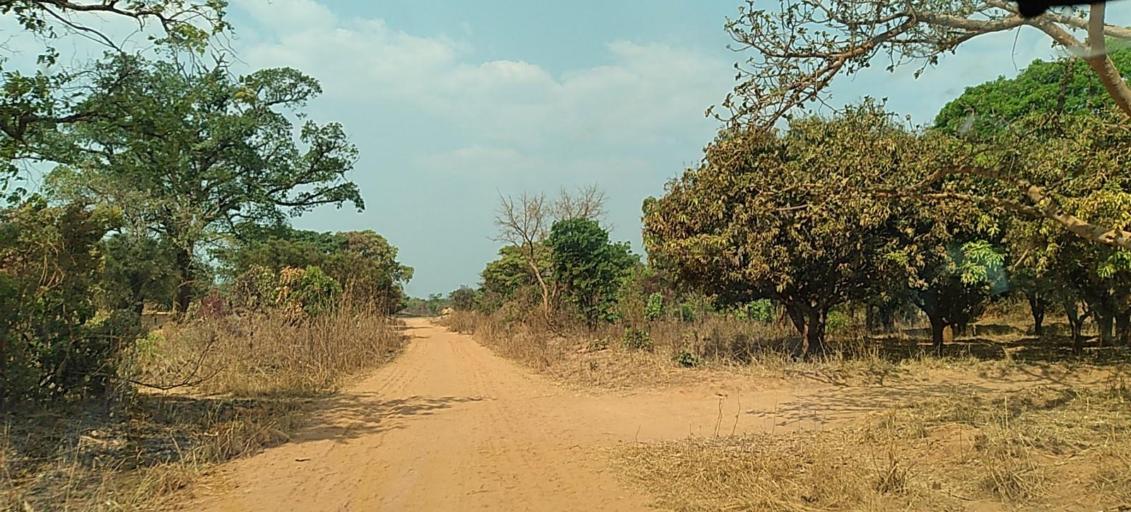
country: ZM
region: North-Western
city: Kasempa
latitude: -13.3053
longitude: 26.0752
